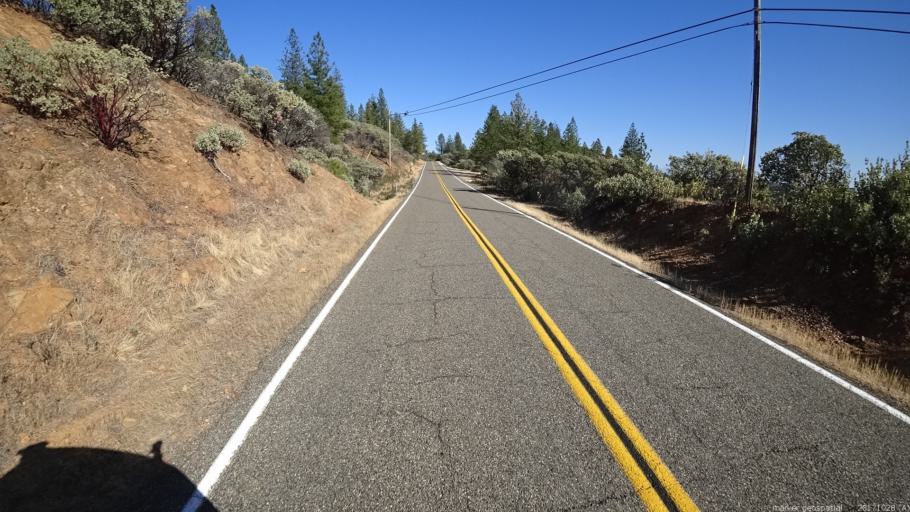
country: US
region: California
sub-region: Shasta County
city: Shasta
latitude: 40.6321
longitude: -122.4612
